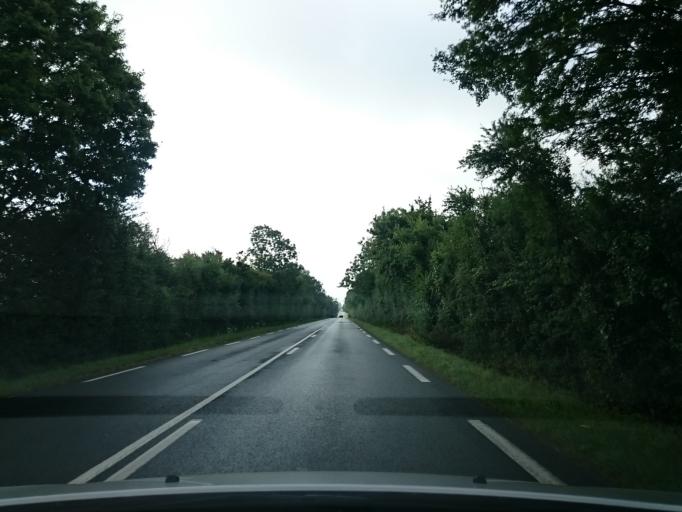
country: FR
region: Lower Normandy
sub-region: Departement du Calvados
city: Cambremer
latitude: 49.1375
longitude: -0.0062
